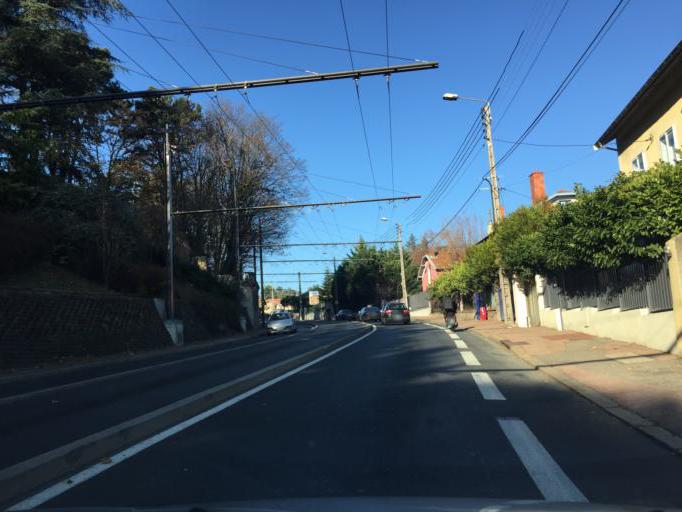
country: FR
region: Rhone-Alpes
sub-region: Departement du Rhone
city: Caluire-et-Cuire
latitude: 45.7959
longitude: 4.8582
